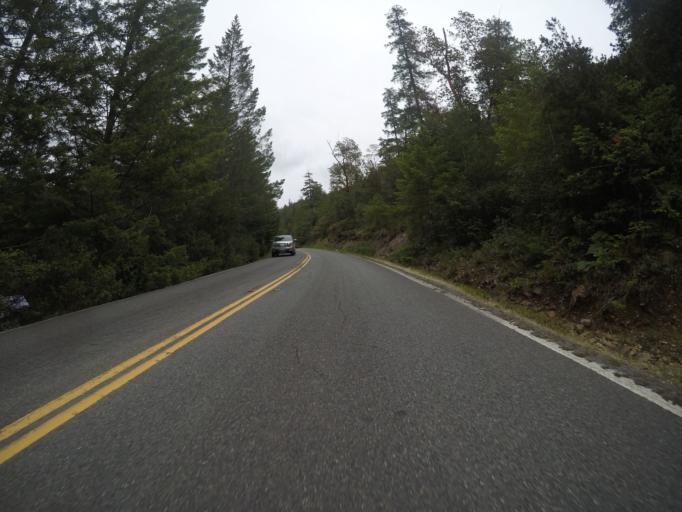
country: US
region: California
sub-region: Del Norte County
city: Bertsch-Oceanview
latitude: 41.7241
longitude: -123.9714
